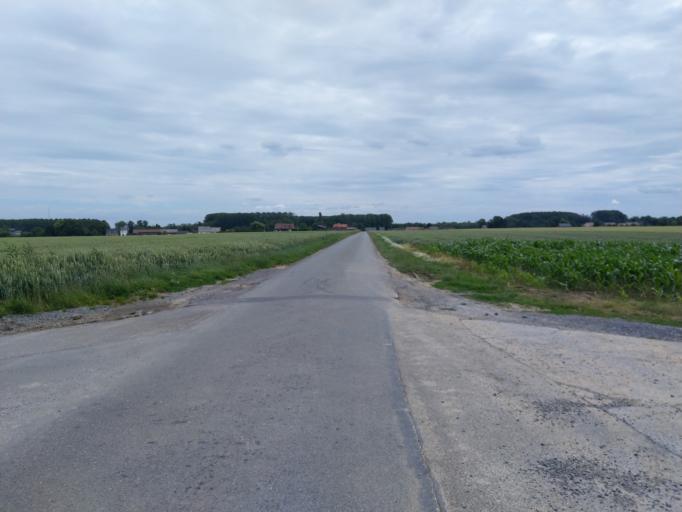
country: BE
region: Wallonia
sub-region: Province du Hainaut
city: Chievres
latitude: 50.5437
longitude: 3.7908
